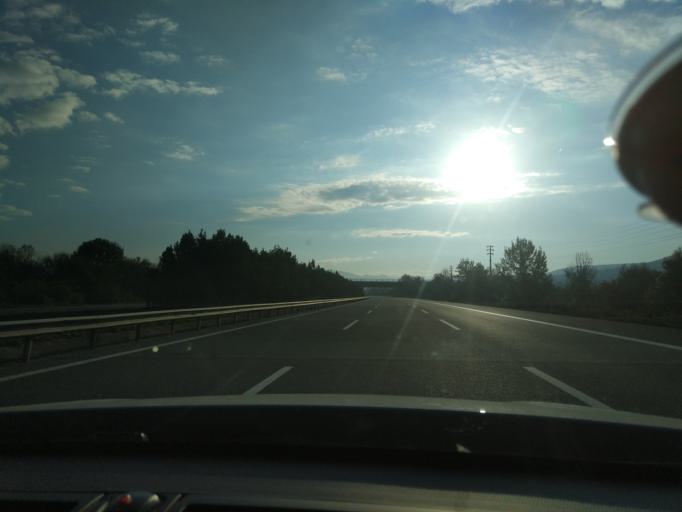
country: TR
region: Duzce
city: Duzce
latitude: 40.7917
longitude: 31.2118
